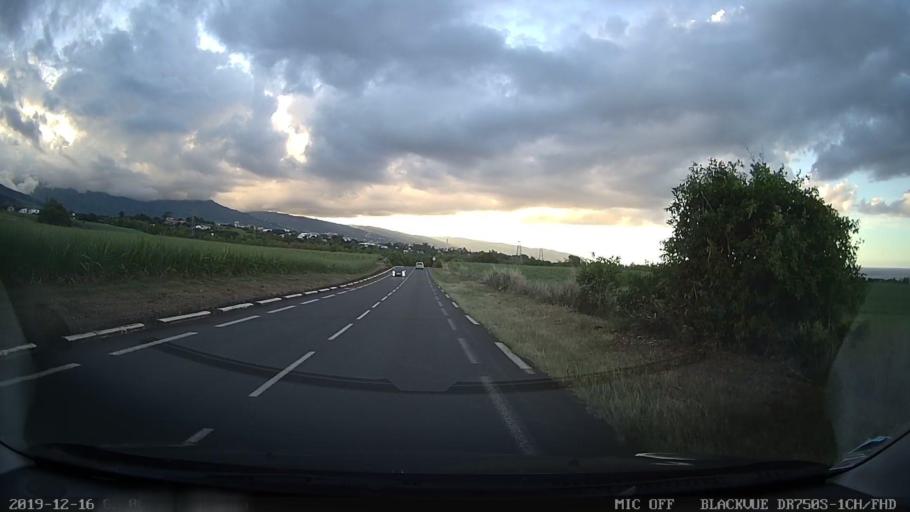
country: RE
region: Reunion
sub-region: Reunion
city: Sainte-Marie
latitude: -20.9160
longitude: 55.5393
